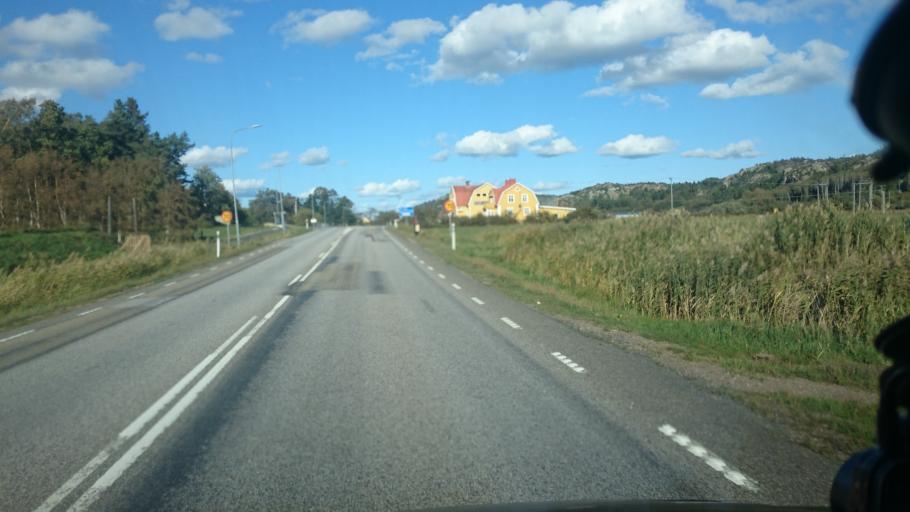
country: SE
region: Vaestra Goetaland
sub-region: Lysekils Kommun
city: Lysekil
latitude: 58.3161
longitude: 11.4851
